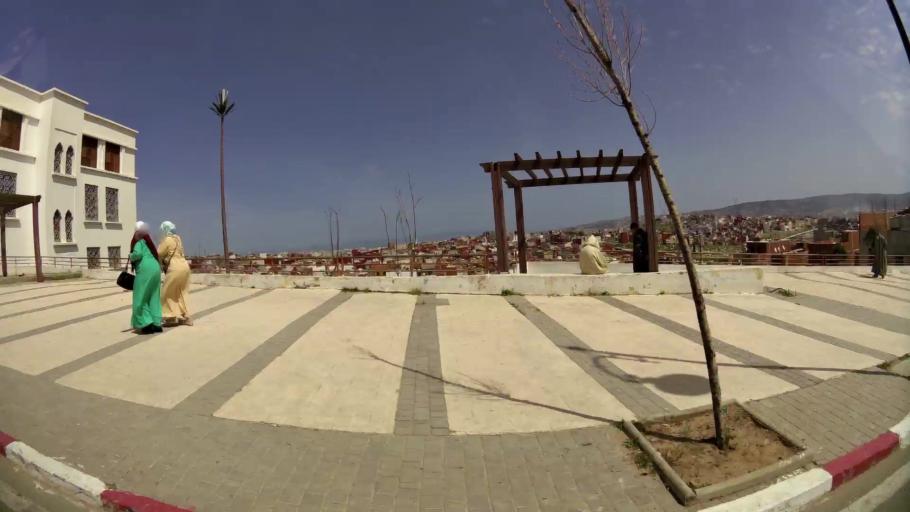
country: MA
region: Tanger-Tetouan
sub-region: Tanger-Assilah
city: Tangier
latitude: 35.7388
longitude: -5.8240
